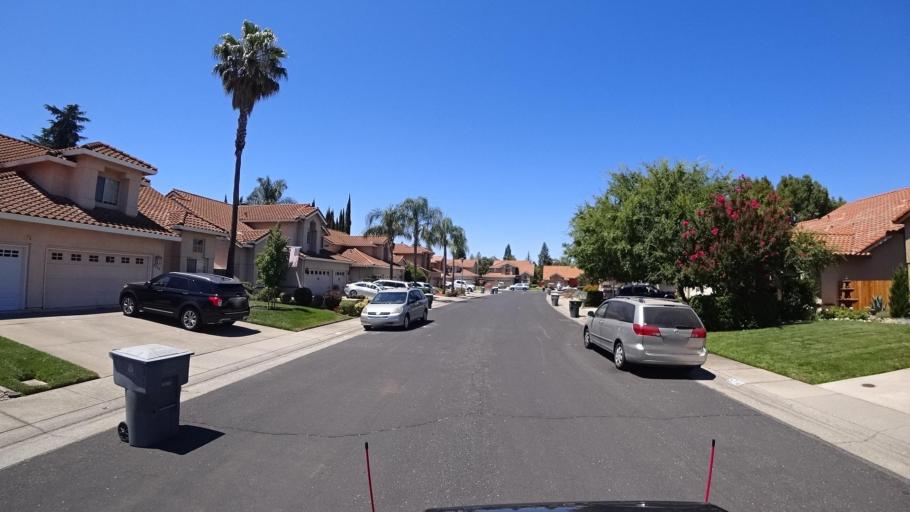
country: US
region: California
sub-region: Placer County
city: Rocklin
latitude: 38.8090
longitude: -121.2664
